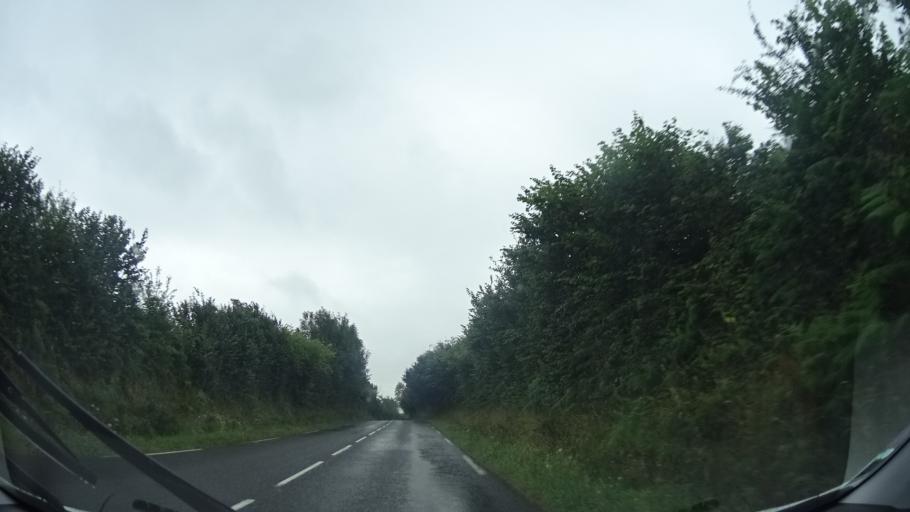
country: FR
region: Lower Normandy
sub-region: Departement de la Manche
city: Beaumont-Hague
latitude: 49.6028
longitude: -1.7823
